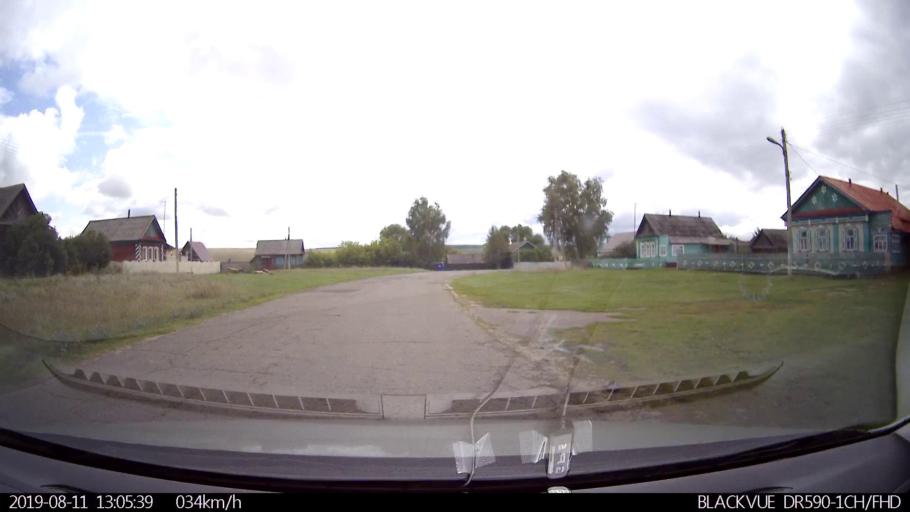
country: RU
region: Ulyanovsk
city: Ignatovka
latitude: 53.8695
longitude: 47.6501
